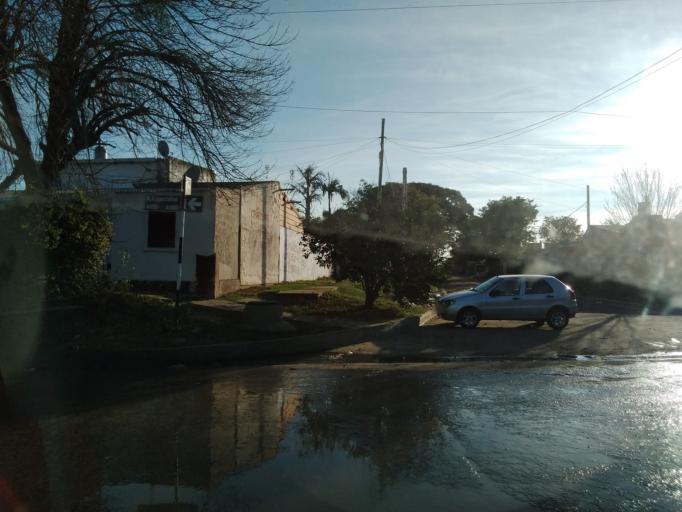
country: AR
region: Corrientes
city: Corrientes
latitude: -27.5017
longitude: -58.8312
